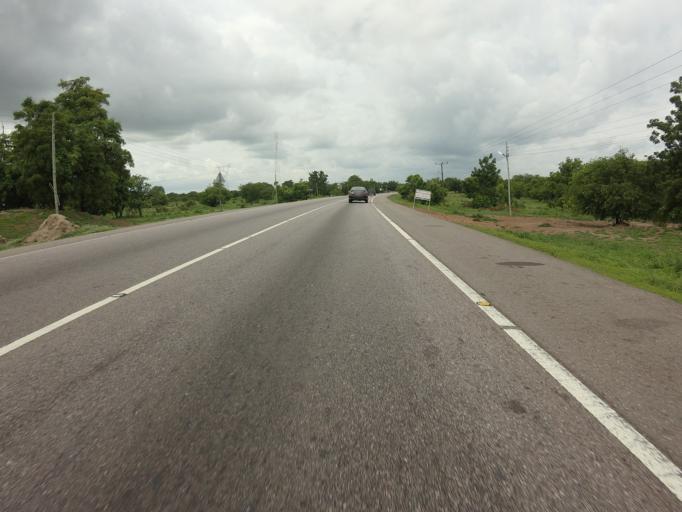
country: GH
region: Northern
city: Tamale
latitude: 8.8888
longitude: -1.4219
